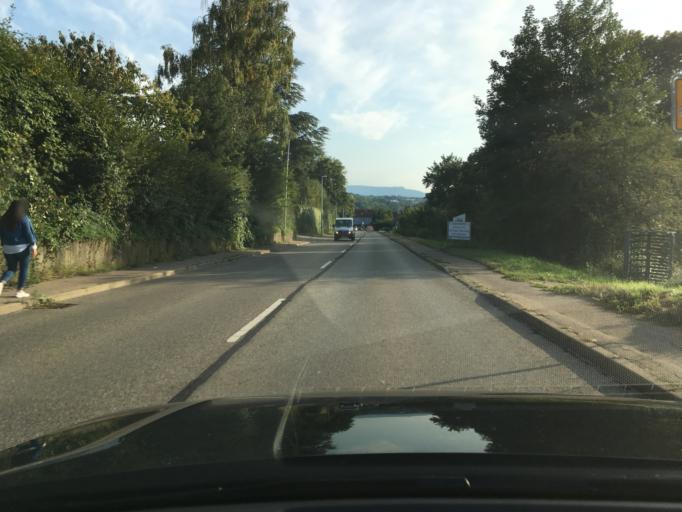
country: DE
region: Baden-Wuerttemberg
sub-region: Regierungsbezirk Stuttgart
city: Uhingen
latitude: 48.7156
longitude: 9.5810
